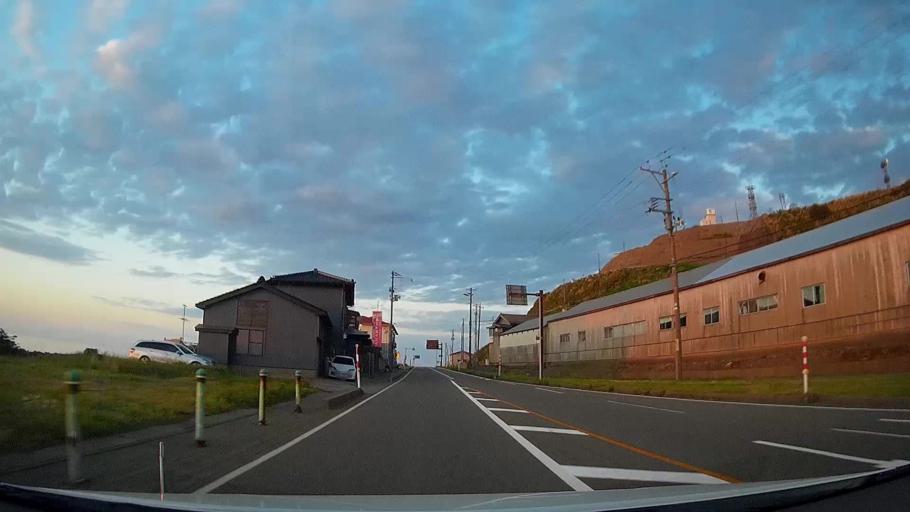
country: JP
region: Niigata
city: Joetsu
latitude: 37.1709
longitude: 138.0934
